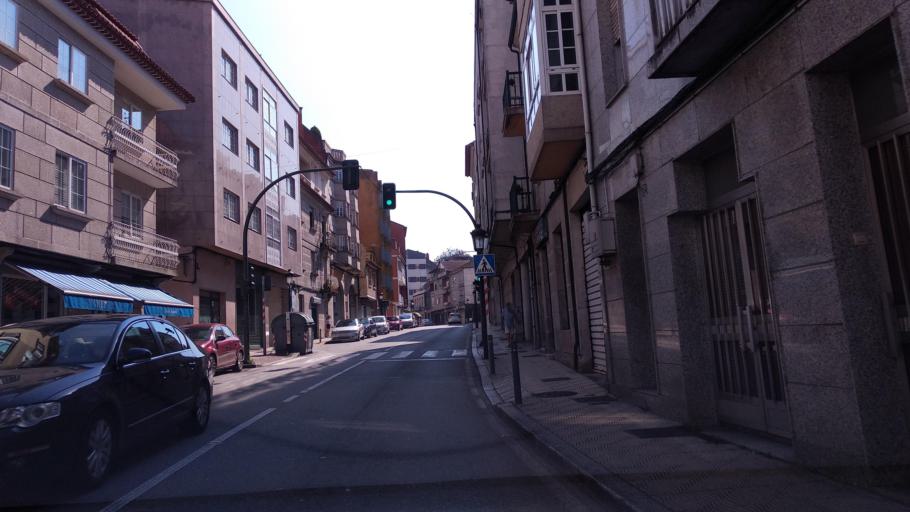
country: ES
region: Galicia
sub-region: Provincia de Pontevedra
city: Moana
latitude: 42.2818
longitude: -8.7364
